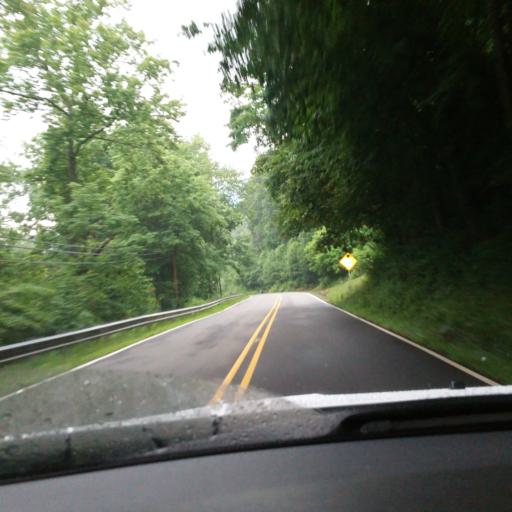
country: US
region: North Carolina
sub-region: Yancey County
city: Burnsville
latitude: 35.8140
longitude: -82.1949
